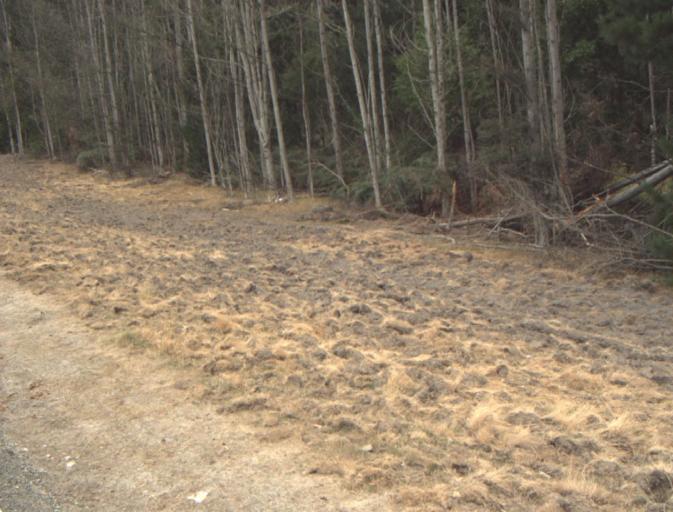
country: AU
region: Tasmania
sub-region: Dorset
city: Bridport
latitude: -41.1604
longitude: 147.2119
